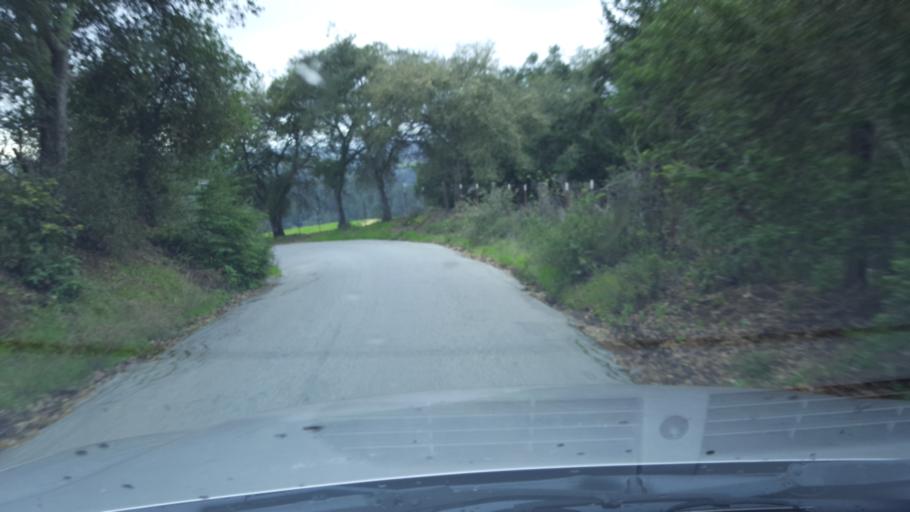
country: US
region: California
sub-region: Santa Cruz County
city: Interlaken
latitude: 37.0013
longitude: -121.7311
